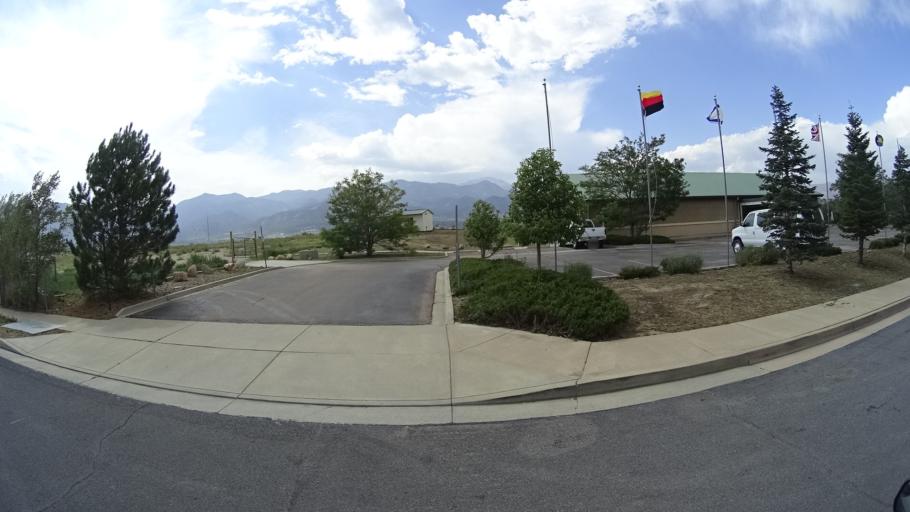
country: US
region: Colorado
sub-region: El Paso County
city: Colorado Springs
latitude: 38.8178
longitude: -104.8084
